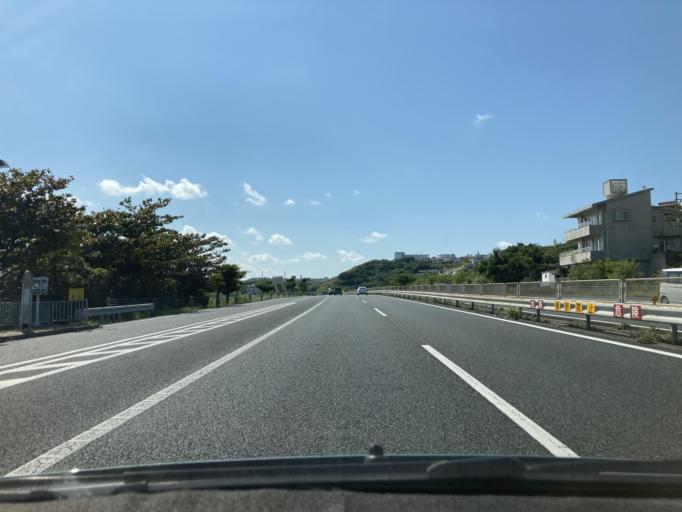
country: JP
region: Okinawa
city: Ginowan
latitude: 26.2395
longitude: 127.7420
